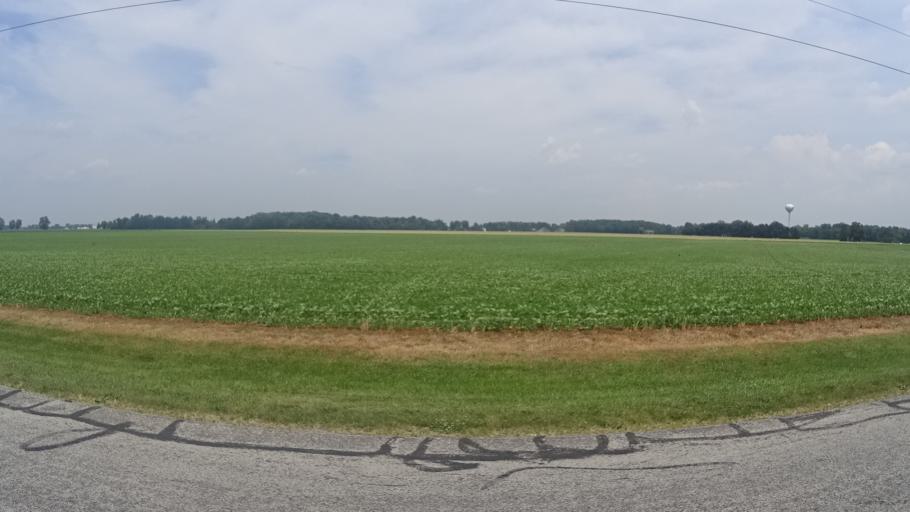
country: US
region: Ohio
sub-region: Erie County
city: Milan
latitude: 41.2990
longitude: -82.6519
